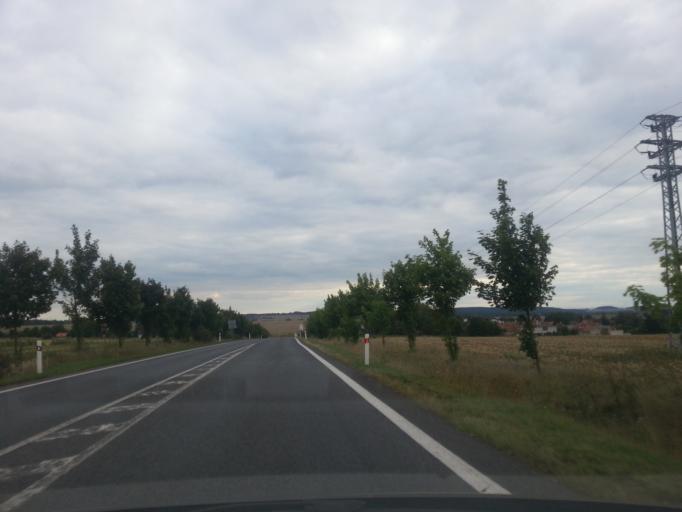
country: CZ
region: Central Bohemia
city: Unhost'
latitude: 50.0897
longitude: 14.1405
